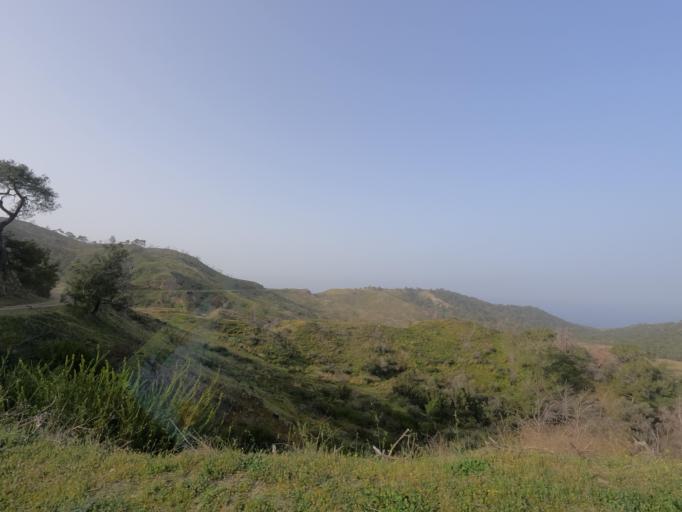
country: CY
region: Pafos
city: Polis
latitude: 35.0012
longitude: 32.3359
